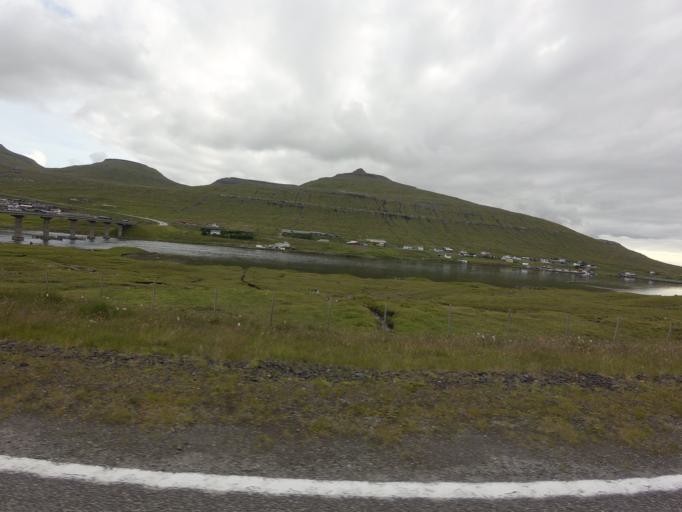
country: FO
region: Eysturoy
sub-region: Eidi
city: Eidi
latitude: 62.2063
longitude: -7.0099
